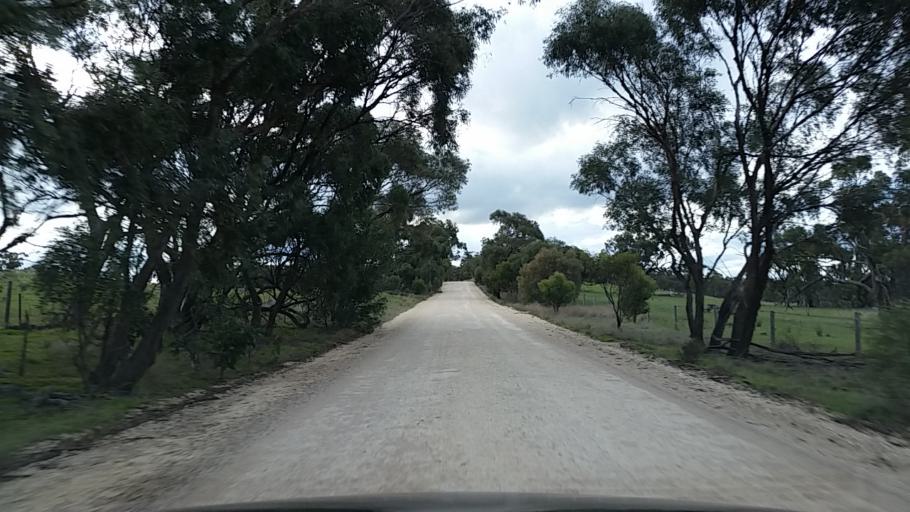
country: AU
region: South Australia
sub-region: Mount Barker
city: Callington
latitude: -35.0030
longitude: 139.0609
